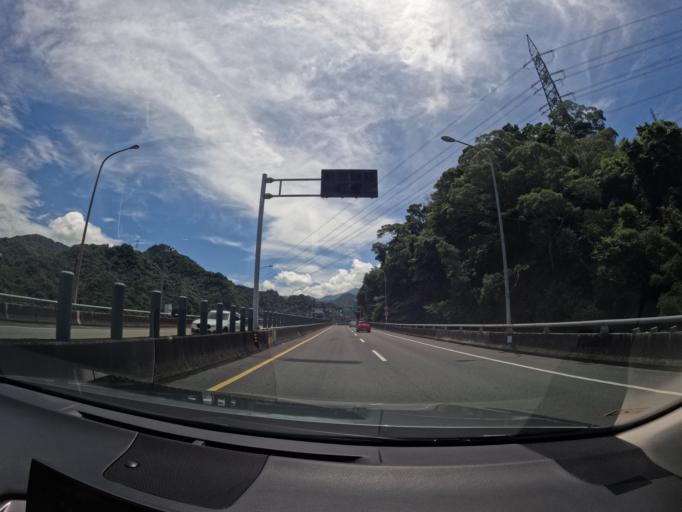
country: TW
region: Taiwan
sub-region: Miaoli
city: Miaoli
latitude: 24.4621
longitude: 120.8683
